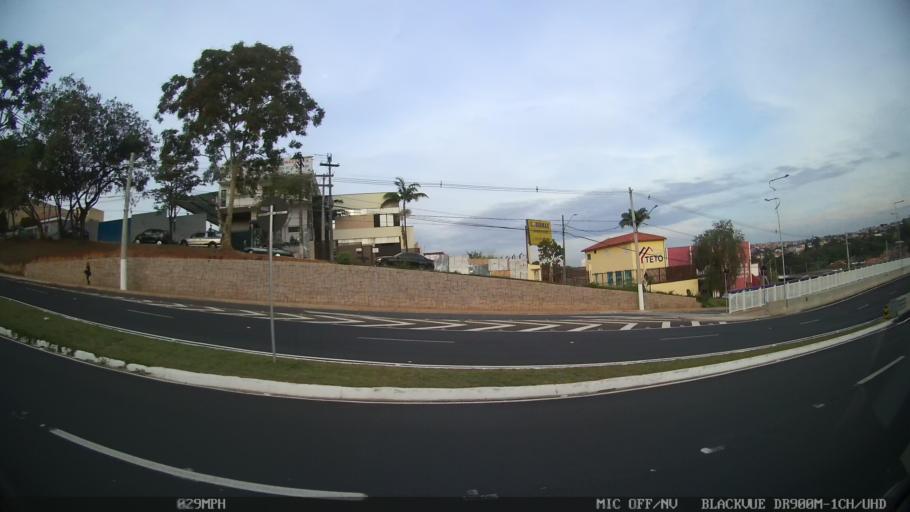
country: BR
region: Sao Paulo
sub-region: Limeira
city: Limeira
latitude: -22.5817
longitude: -47.4092
